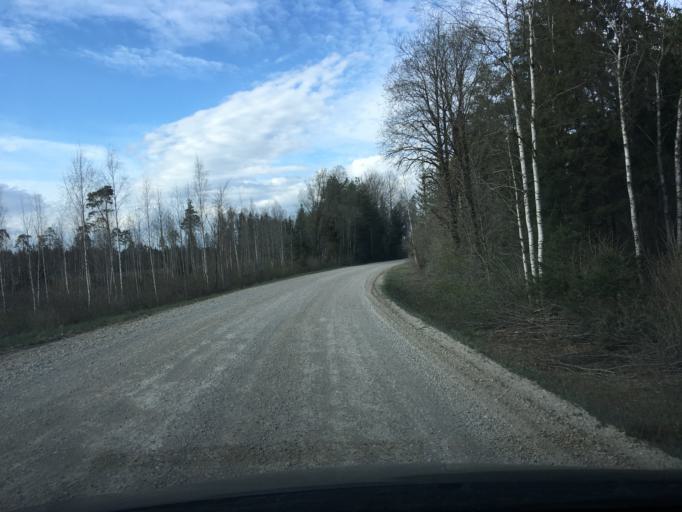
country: EE
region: Raplamaa
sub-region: Maerjamaa vald
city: Marjamaa
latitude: 58.9575
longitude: 24.3261
